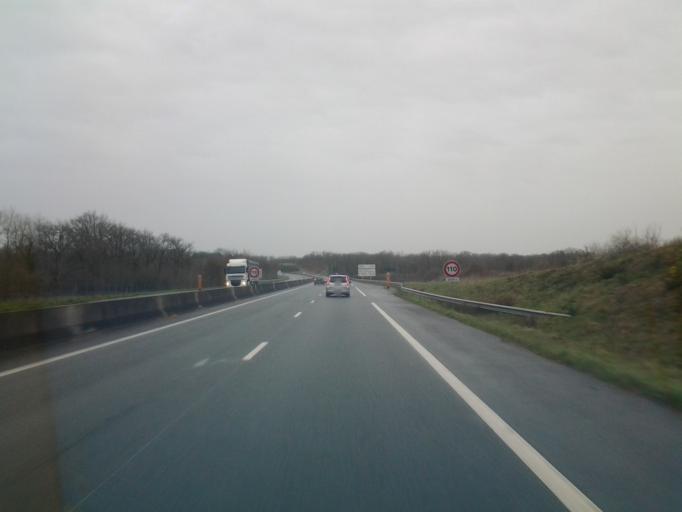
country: FR
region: Pays de la Loire
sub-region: Departement de la Vendee
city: Les Clouzeaux
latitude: 46.6399
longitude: -1.5000
